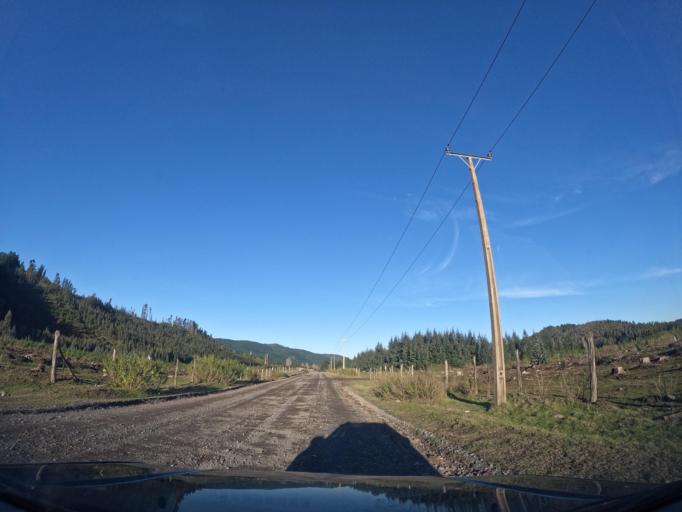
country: CL
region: Biobio
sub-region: Provincia de Concepcion
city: Chiguayante
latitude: -37.0788
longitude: -72.9309
